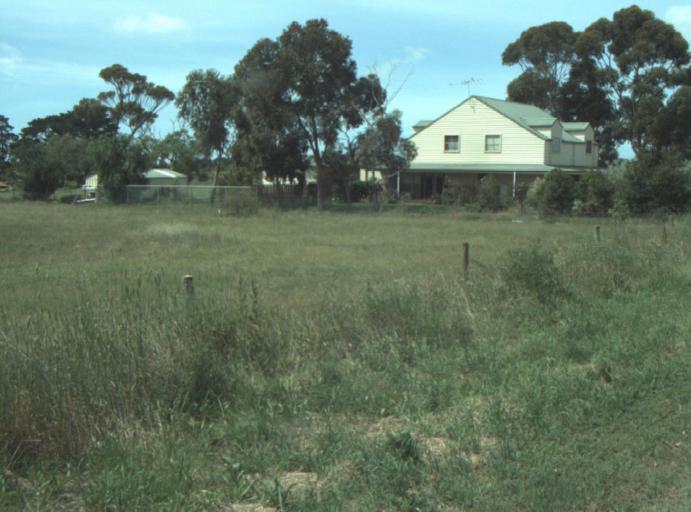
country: AU
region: Victoria
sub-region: Wyndham
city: Little River
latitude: -37.9629
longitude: 144.5078
